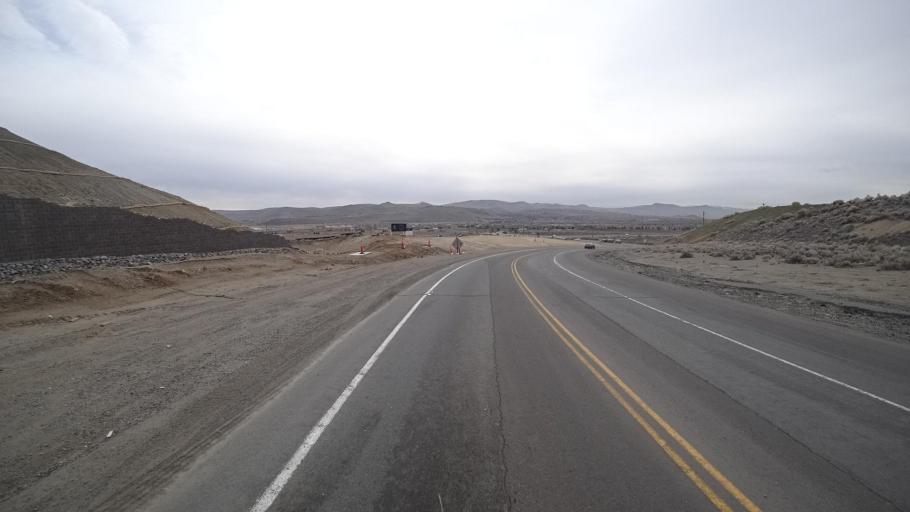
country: US
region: Nevada
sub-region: Washoe County
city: Sun Valley
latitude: 39.6111
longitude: -119.7346
